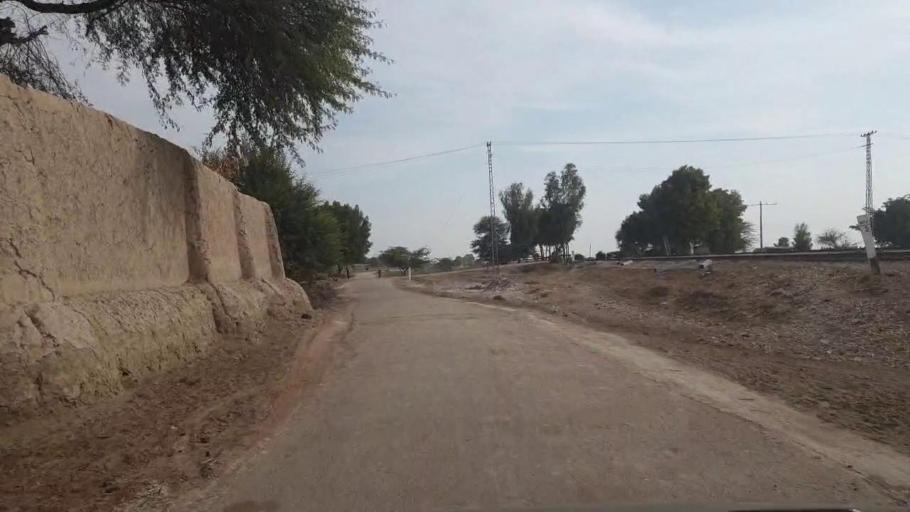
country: PK
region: Sindh
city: Shahpur Chakar
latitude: 26.0816
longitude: 68.4925
